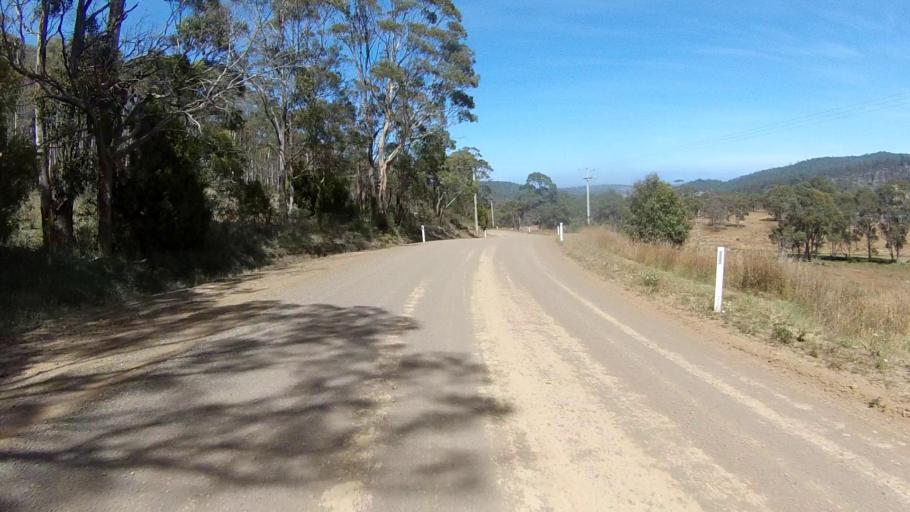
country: AU
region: Tasmania
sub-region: Sorell
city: Sorell
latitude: -42.7440
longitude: 147.7301
